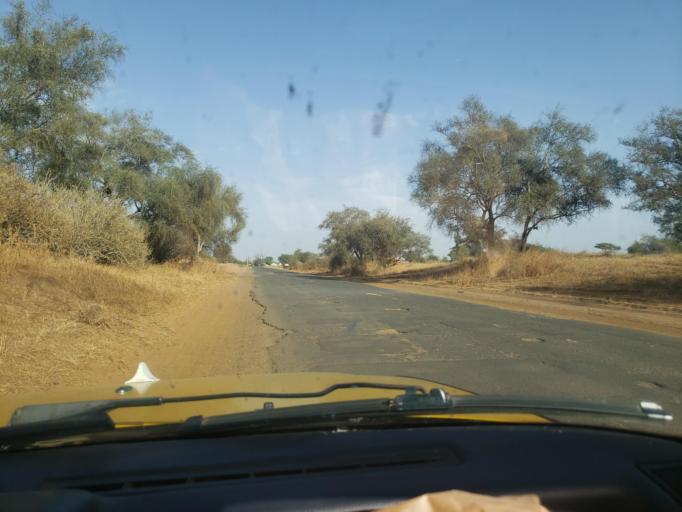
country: SN
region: Louga
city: Louga
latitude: 15.5123
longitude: -16.0019
